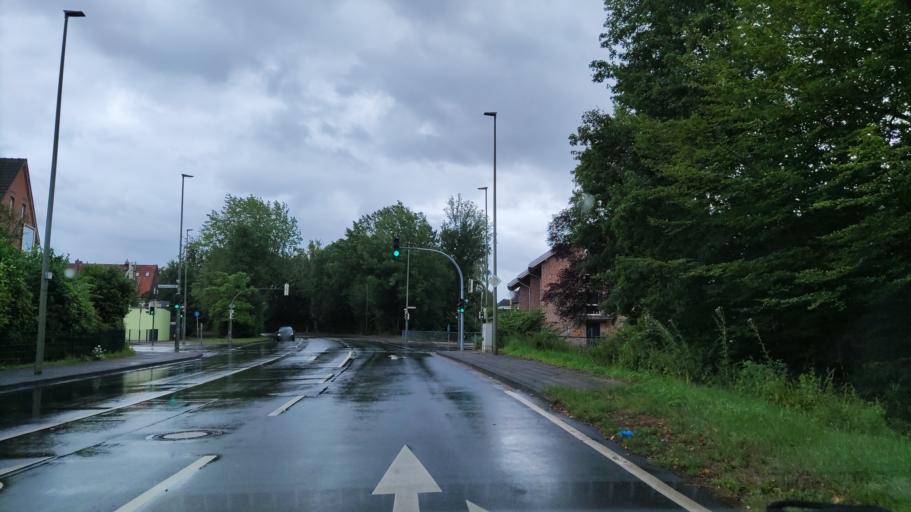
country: DE
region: North Rhine-Westphalia
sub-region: Regierungsbezirk Arnsberg
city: Hamm
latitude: 51.7051
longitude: 7.8385
